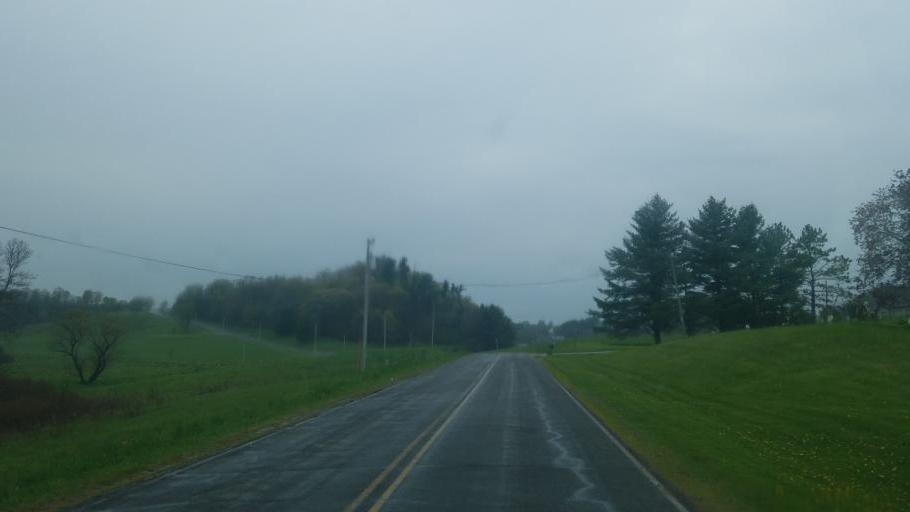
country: US
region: Wisconsin
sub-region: Juneau County
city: Elroy
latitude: 43.6542
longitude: -90.2355
